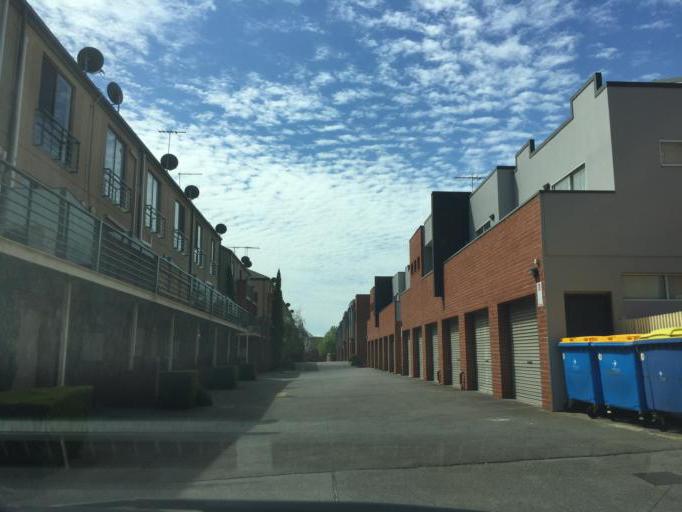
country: AU
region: Victoria
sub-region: Maribyrnong
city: Maidstone
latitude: -37.7740
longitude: 144.8800
